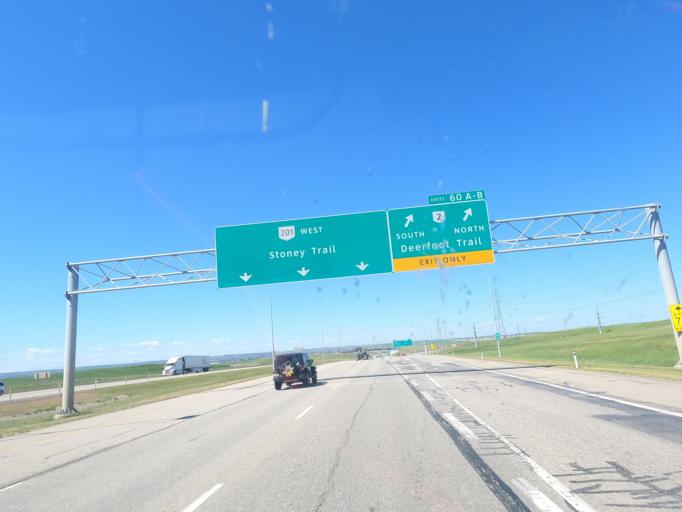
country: CA
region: Alberta
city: Airdrie
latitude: 51.1759
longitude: -113.9830
